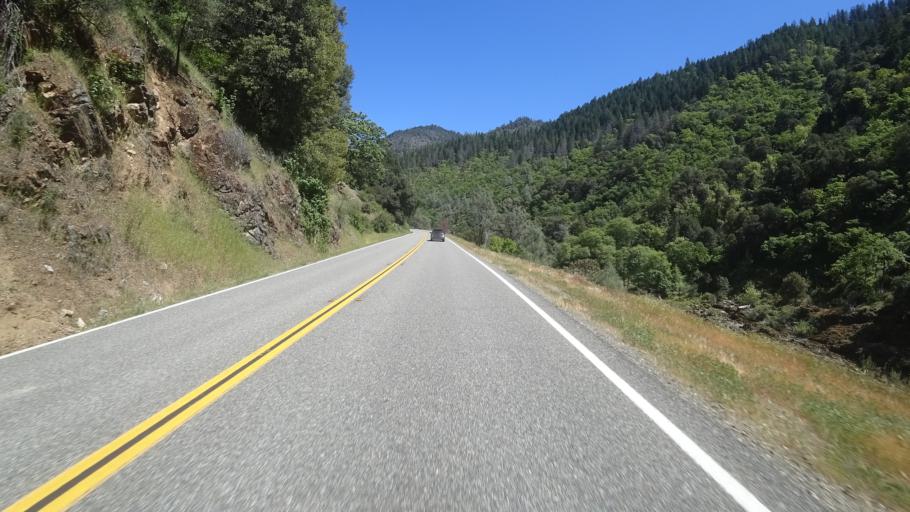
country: US
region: California
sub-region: Trinity County
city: Hayfork
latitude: 40.7352
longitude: -123.1982
